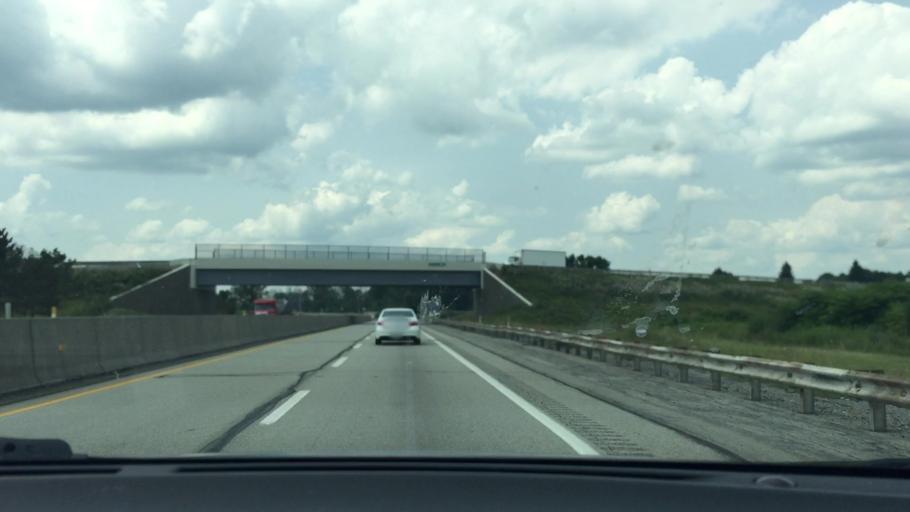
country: US
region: Pennsylvania
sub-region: Somerset County
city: Somerset
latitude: 40.0373
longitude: -79.1016
